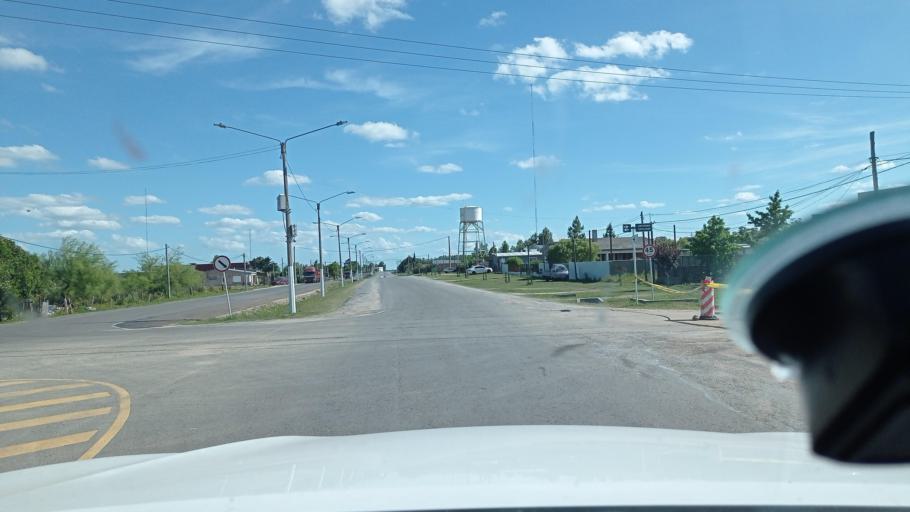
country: UY
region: Florida
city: Florida
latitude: -34.0851
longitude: -56.2370
